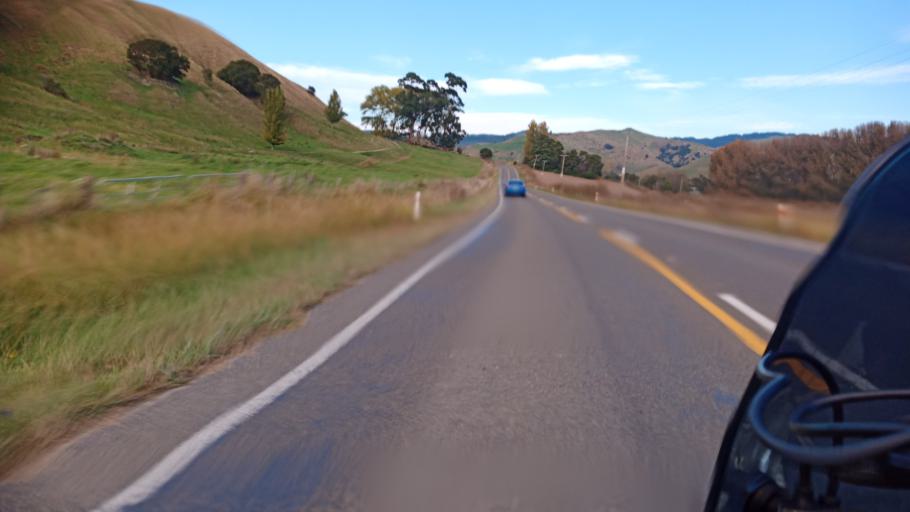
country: NZ
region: Gisborne
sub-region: Gisborne District
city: Gisborne
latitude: -38.7947
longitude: 177.9098
